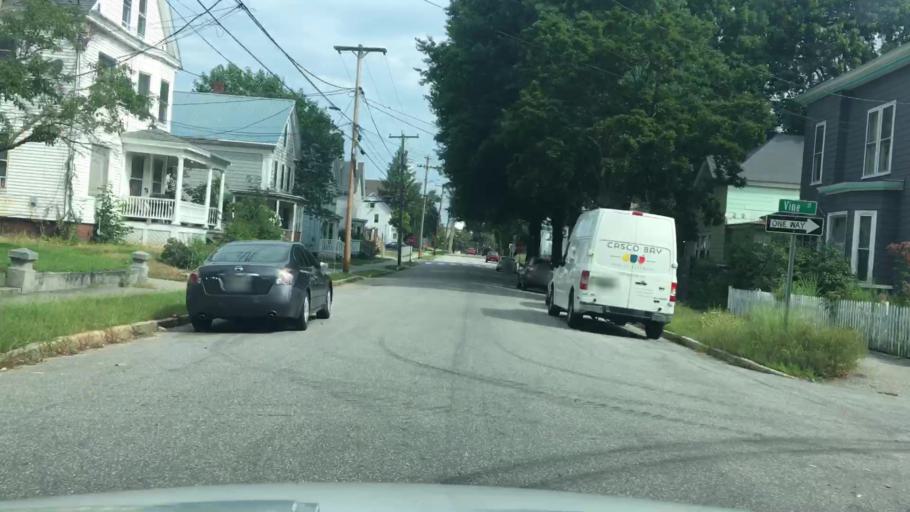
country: US
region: Maine
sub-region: Androscoggin County
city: Auburn
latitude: 44.0945
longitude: -70.2277
